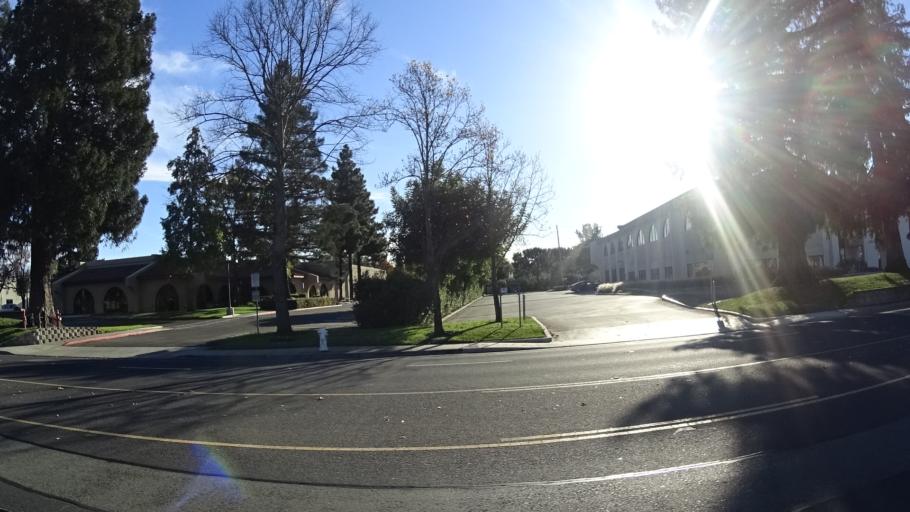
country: US
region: California
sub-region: Santa Clara County
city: Santa Clara
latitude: 37.3697
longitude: -121.9701
